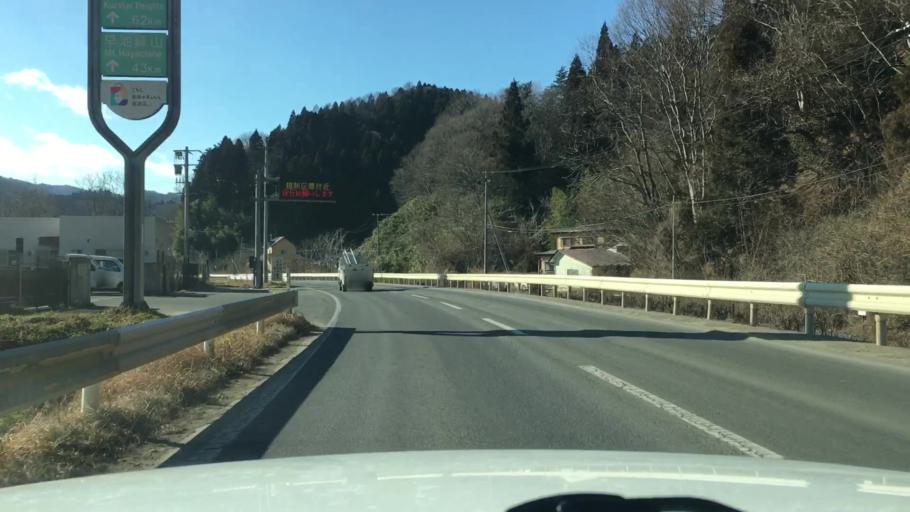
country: JP
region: Iwate
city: Miyako
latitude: 39.6326
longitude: 141.8816
